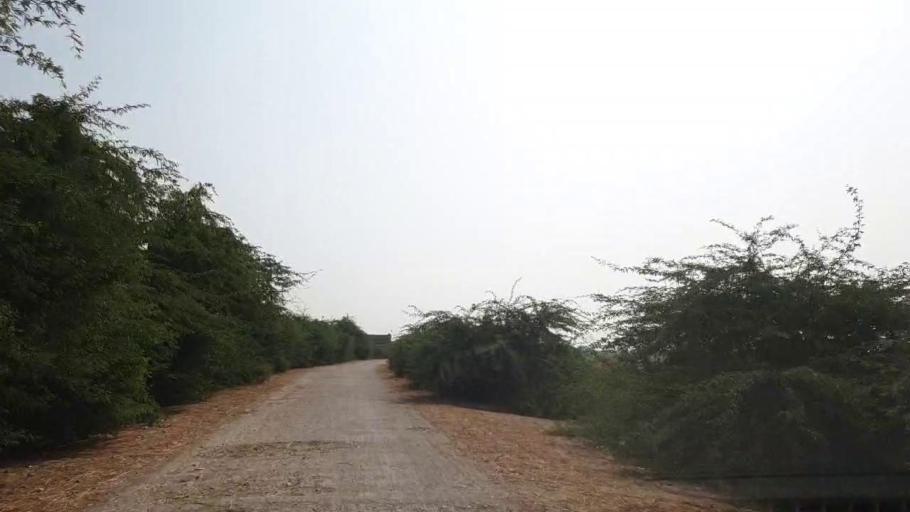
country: PK
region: Sindh
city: Matli
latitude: 25.0036
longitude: 68.5731
